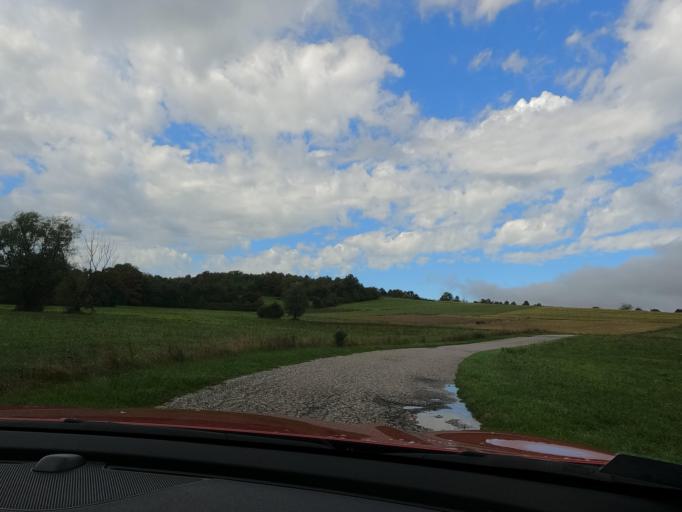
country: HR
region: Sisacko-Moslavacka
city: Petrinja
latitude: 45.3336
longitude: 16.2158
